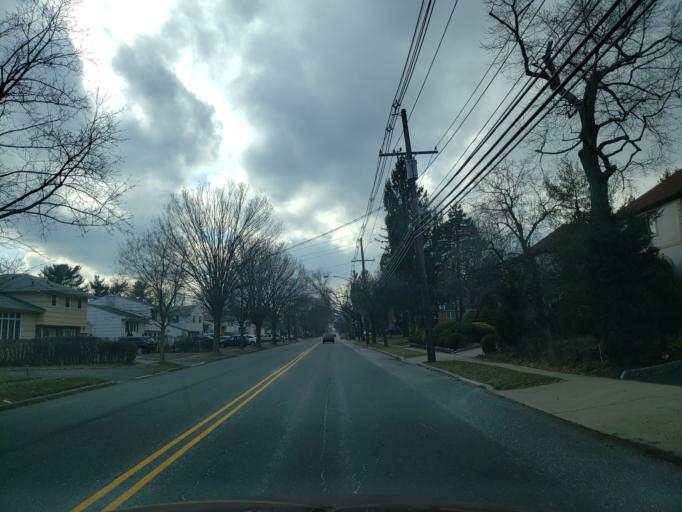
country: US
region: New Jersey
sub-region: Union County
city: Springfield
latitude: 40.7001
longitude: -74.3220
